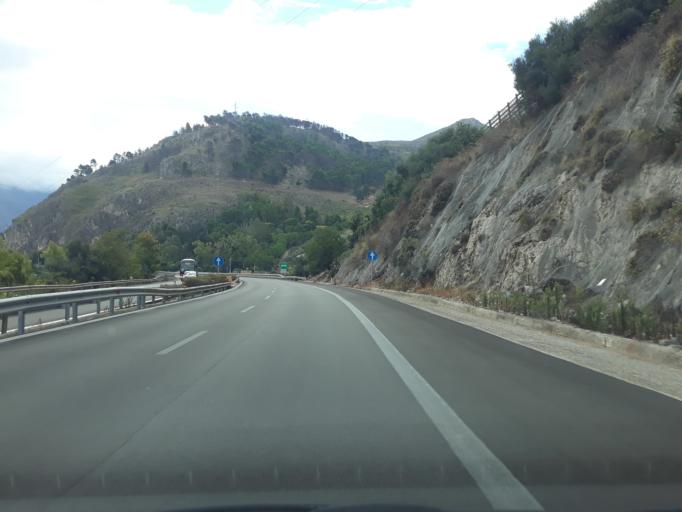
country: IT
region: Sicily
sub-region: Palermo
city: Trabia
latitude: 37.9882
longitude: 13.6552
